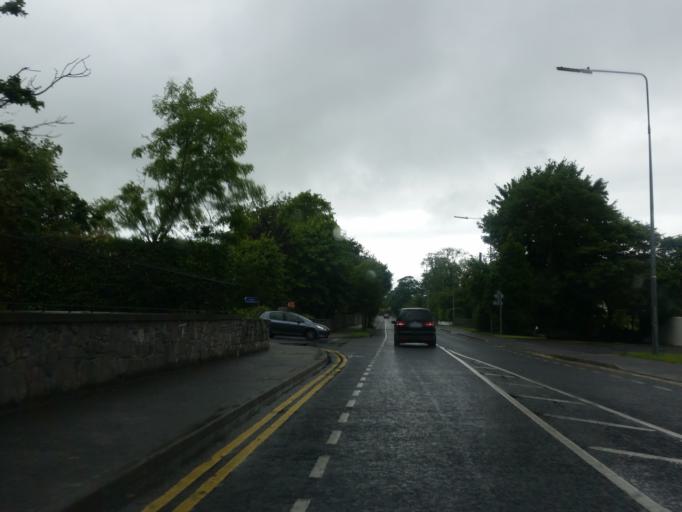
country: IE
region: Connaught
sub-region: Sligo
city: Sligo
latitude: 54.2712
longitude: -8.4975
